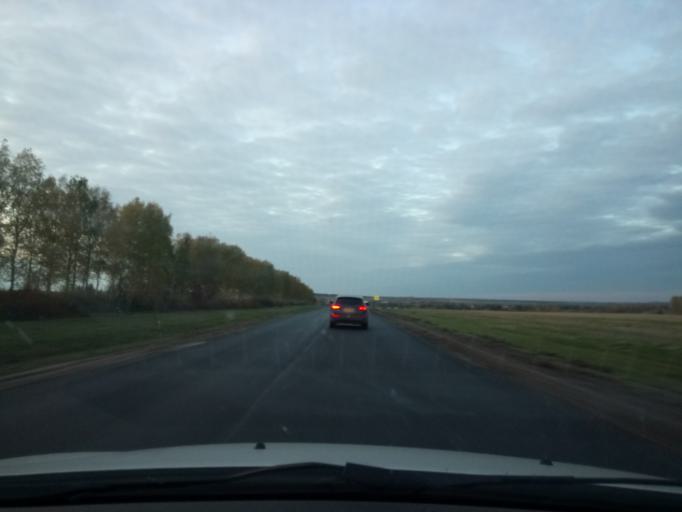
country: RU
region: Nizjnij Novgorod
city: Bol'shoye Murashkino
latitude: 55.8705
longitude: 44.7483
